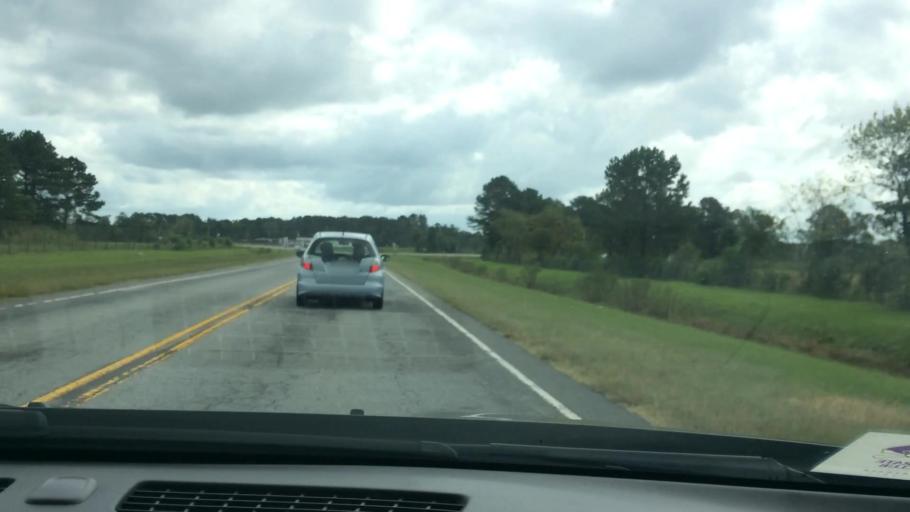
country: US
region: North Carolina
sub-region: Pitt County
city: Farmville
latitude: 35.6097
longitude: -77.6571
